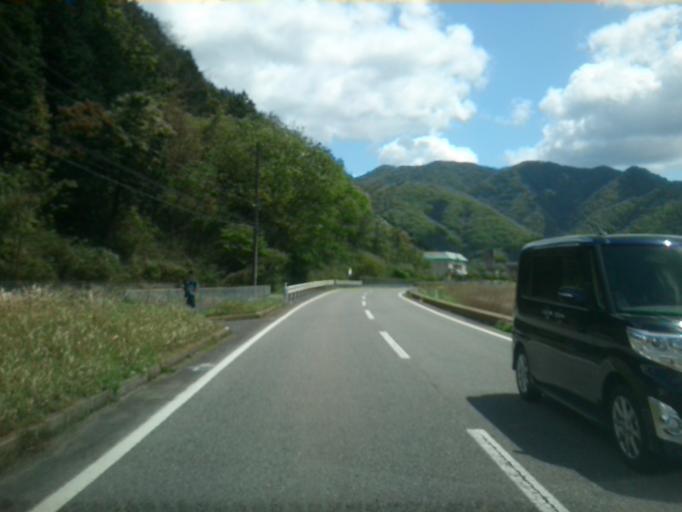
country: JP
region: Hyogo
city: Toyooka
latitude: 35.4551
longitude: 134.8715
